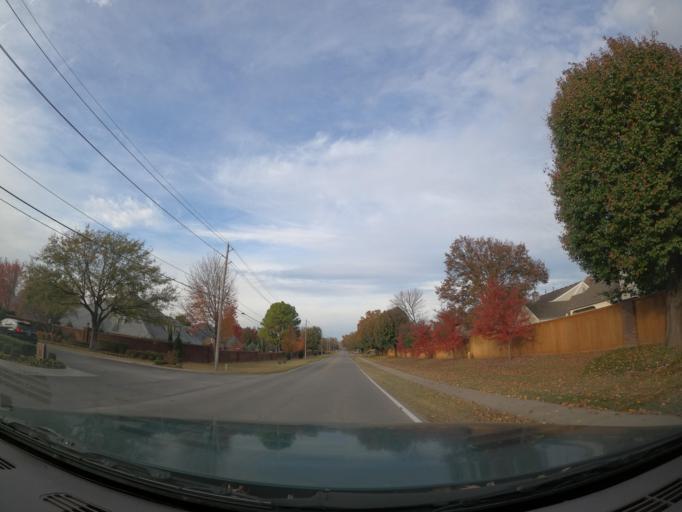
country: US
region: Oklahoma
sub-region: Tulsa County
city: Jenks
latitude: 36.0371
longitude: -95.9400
